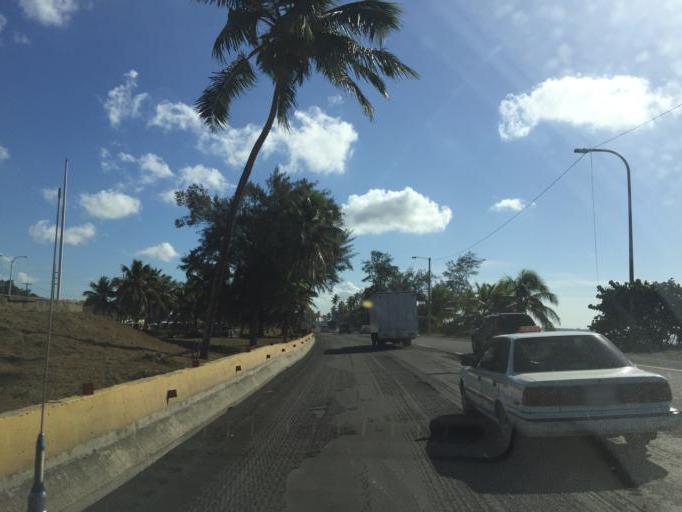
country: DO
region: Santo Domingo
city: Guerra
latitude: 18.4562
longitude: -69.7153
